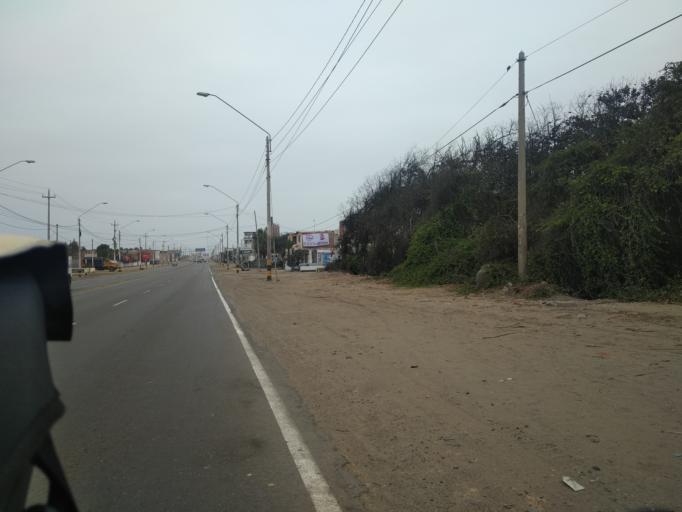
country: PE
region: La Libertad
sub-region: Provincia de Trujillo
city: Huanchaco
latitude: -8.0880
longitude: -79.1020
